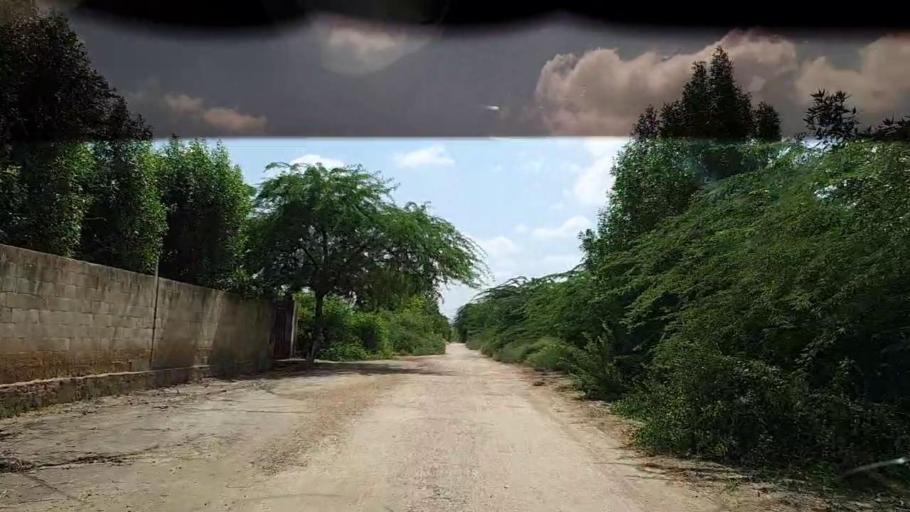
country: PK
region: Sindh
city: Kadhan
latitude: 24.5889
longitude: 68.9582
